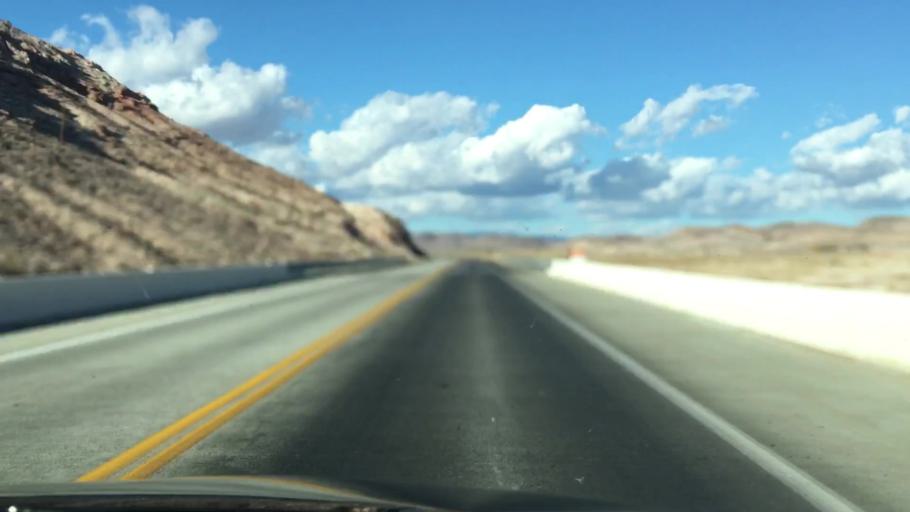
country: US
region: Nevada
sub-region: Nye County
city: Beatty
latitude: 36.9766
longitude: -116.7236
